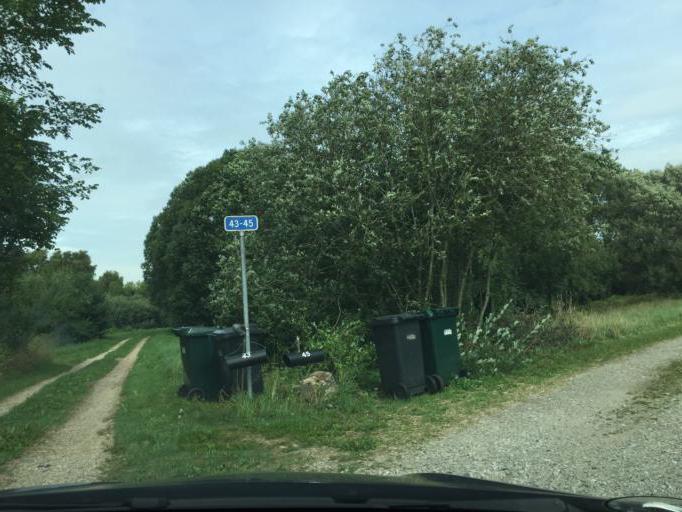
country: DK
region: South Denmark
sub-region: Assens Kommune
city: Vissenbjerg
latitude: 55.3591
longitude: 10.1161
